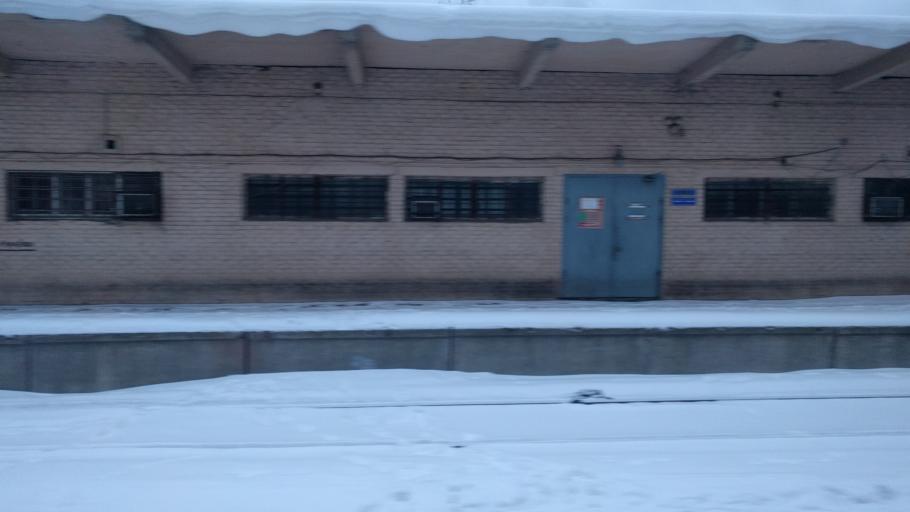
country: RU
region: Moscow
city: Sokol'niki
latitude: 55.7843
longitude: 37.6494
